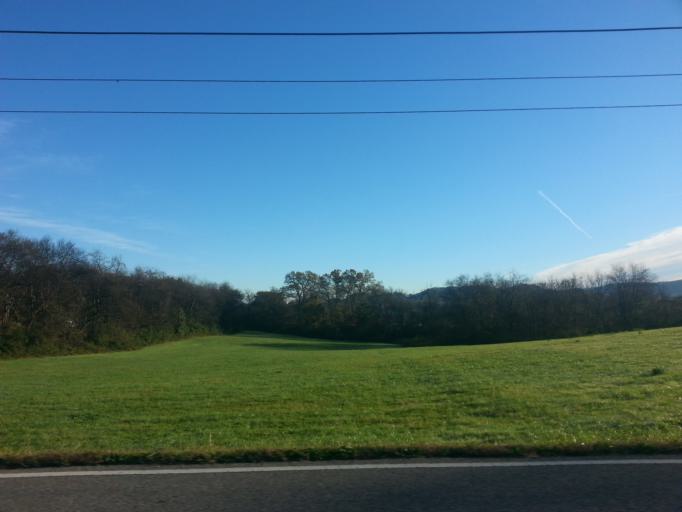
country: US
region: Tennessee
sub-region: Blount County
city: Eagleton Village
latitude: 35.8335
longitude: -83.9555
